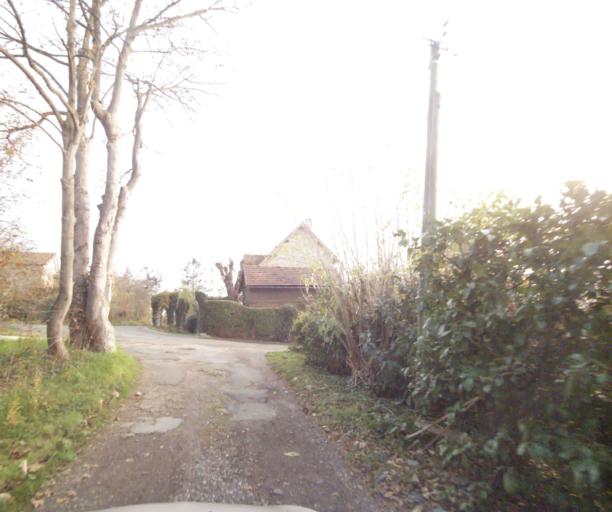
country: FR
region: Ile-de-France
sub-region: Departement des Yvelines
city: Triel-sur-Seine
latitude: 48.9848
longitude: 2.0078
